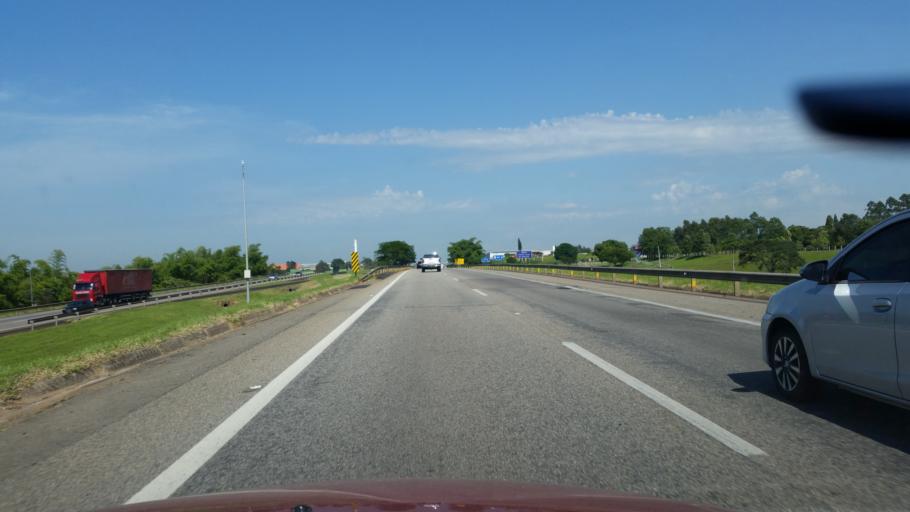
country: BR
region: Sao Paulo
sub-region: Boituva
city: Boituva
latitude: -23.2983
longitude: -47.6757
